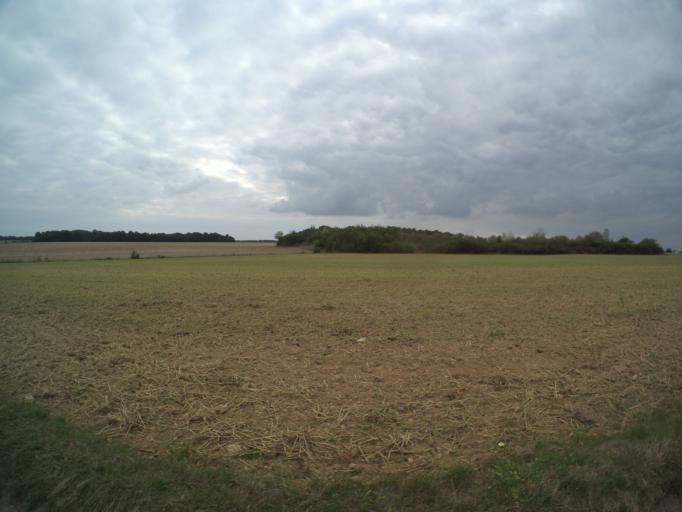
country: FR
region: Centre
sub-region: Departement d'Indre-et-Loire
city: Reugny
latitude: 47.4786
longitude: 0.9158
